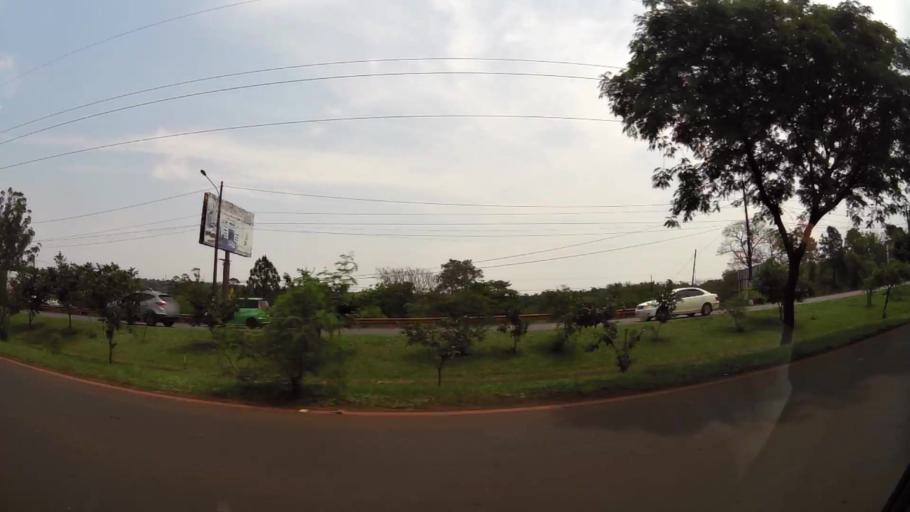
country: PY
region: Alto Parana
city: Ciudad del Este
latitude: -25.4836
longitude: -54.6273
